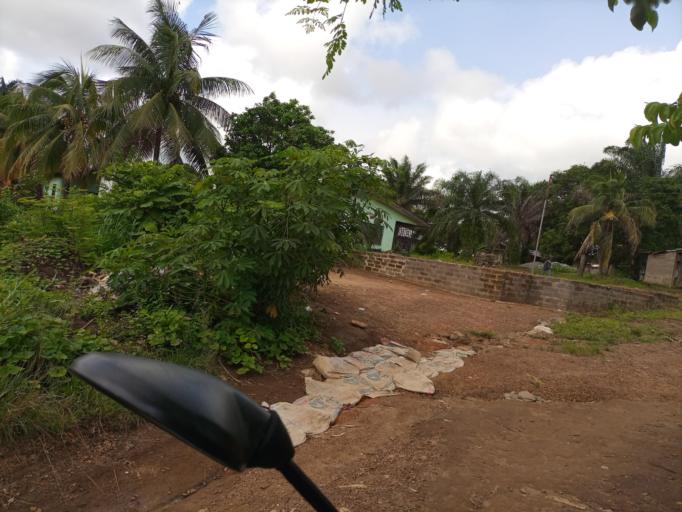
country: SL
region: Southern Province
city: Bo
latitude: 7.9688
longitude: -11.7623
